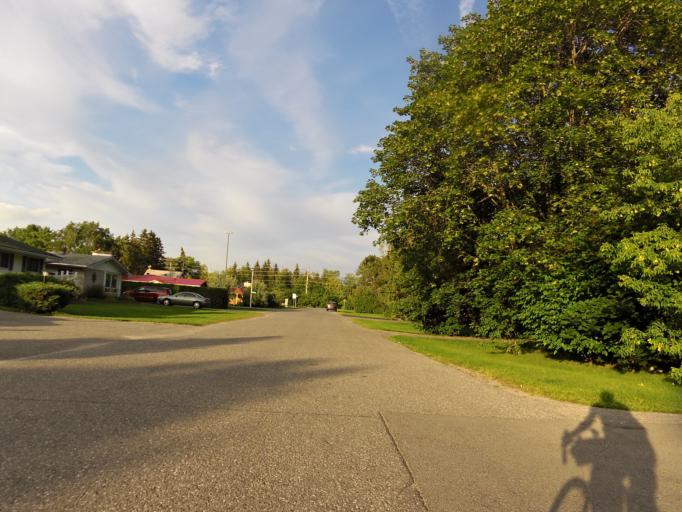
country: CA
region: Ontario
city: Bells Corners
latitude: 45.3293
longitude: -75.8114
